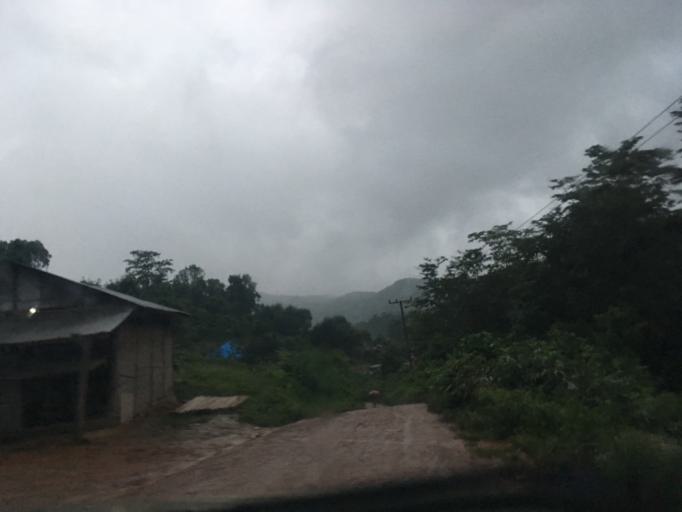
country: LA
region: Oudomxai
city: Muang La
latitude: 21.2550
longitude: 101.9308
